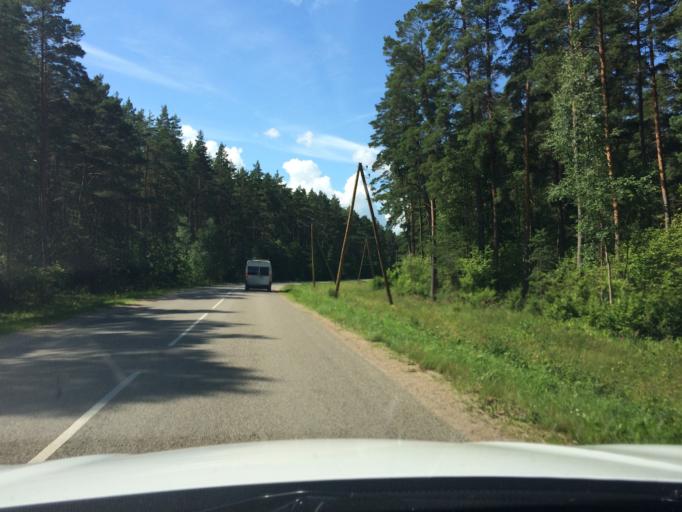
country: LV
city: Tervete
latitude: 56.4902
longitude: 23.4363
